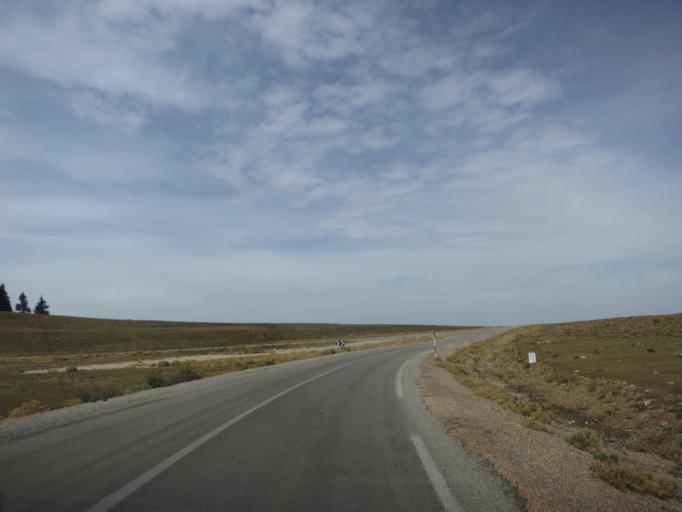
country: MA
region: Meknes-Tafilalet
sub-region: Ifrane
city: Azrou
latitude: 33.3678
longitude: -5.1399
